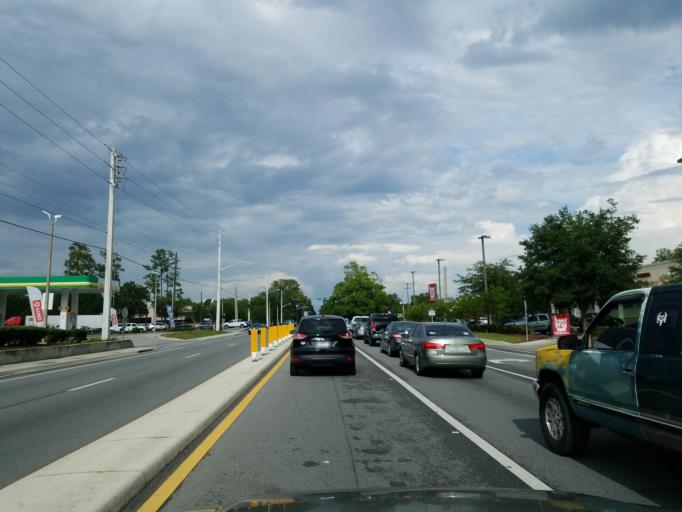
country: US
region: Florida
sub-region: Marion County
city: Ocala
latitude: 29.2231
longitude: -82.1487
